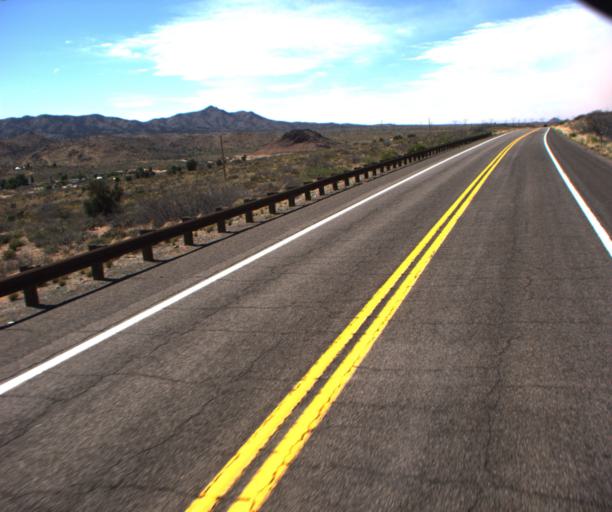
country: US
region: Arizona
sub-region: Mohave County
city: Peach Springs
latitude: 35.3696
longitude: -113.7158
